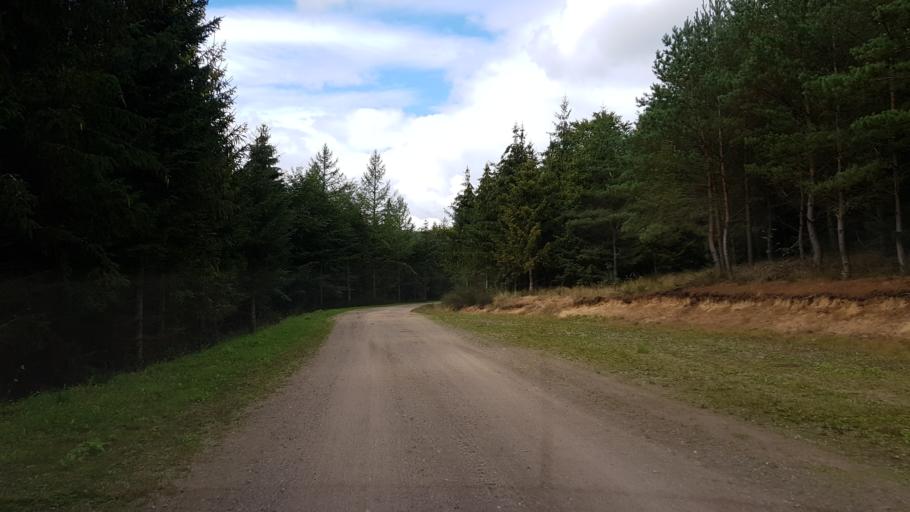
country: PL
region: West Pomeranian Voivodeship
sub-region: Powiat bialogardzki
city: Tychowo
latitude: 53.9720
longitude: 16.3830
